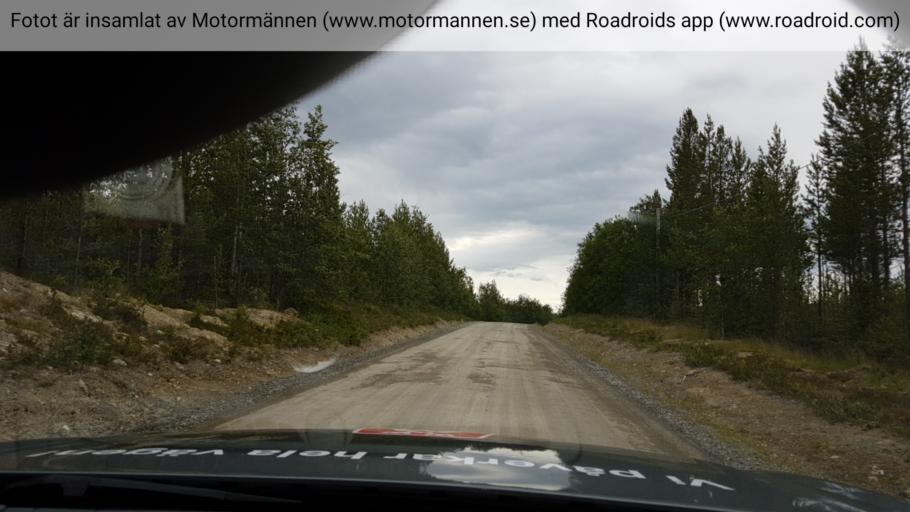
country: SE
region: Jaemtland
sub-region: Bergs Kommun
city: Hoverberg
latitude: 62.7784
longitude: 13.8262
